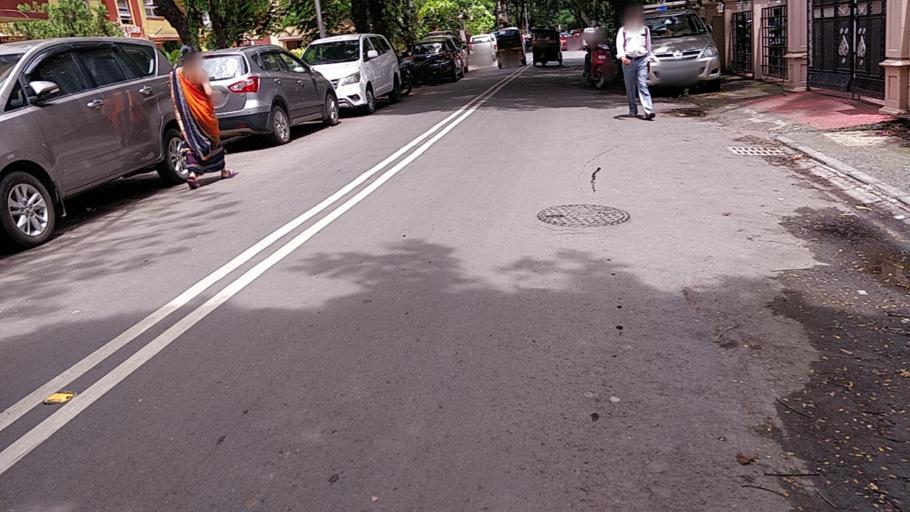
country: IN
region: Maharashtra
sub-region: Mumbai Suburban
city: Mumbai
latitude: 19.0600
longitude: 72.8338
